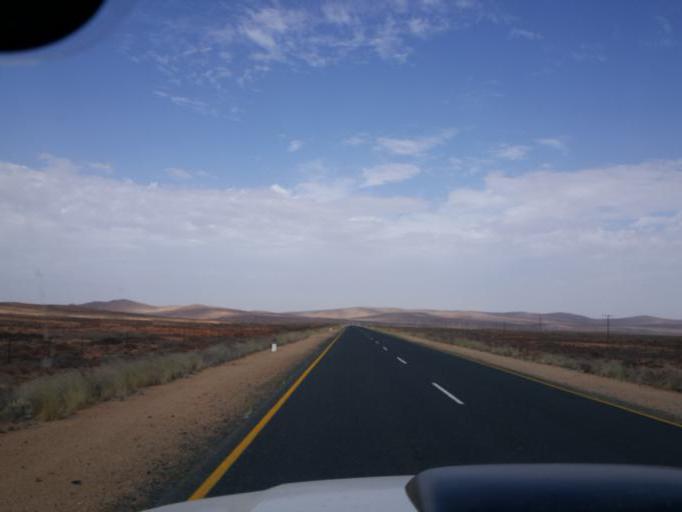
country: ZA
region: Northern Cape
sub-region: Namakwa District Municipality
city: Springbok
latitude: -29.2589
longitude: 17.4598
